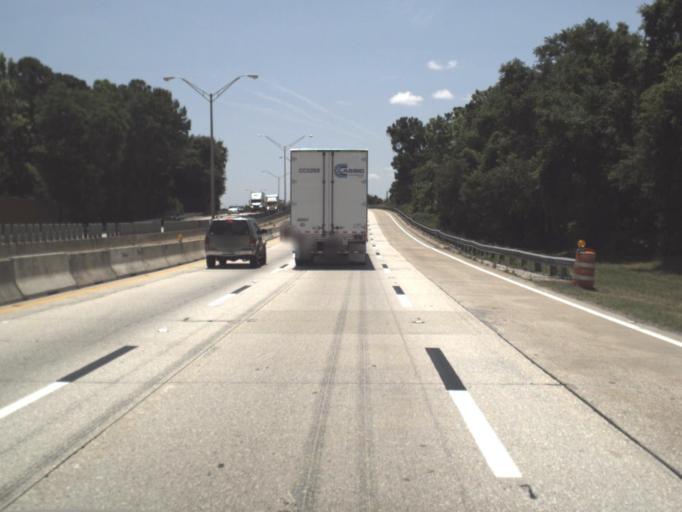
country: US
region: Florida
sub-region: Duval County
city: Jacksonville
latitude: 30.3019
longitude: -81.6410
